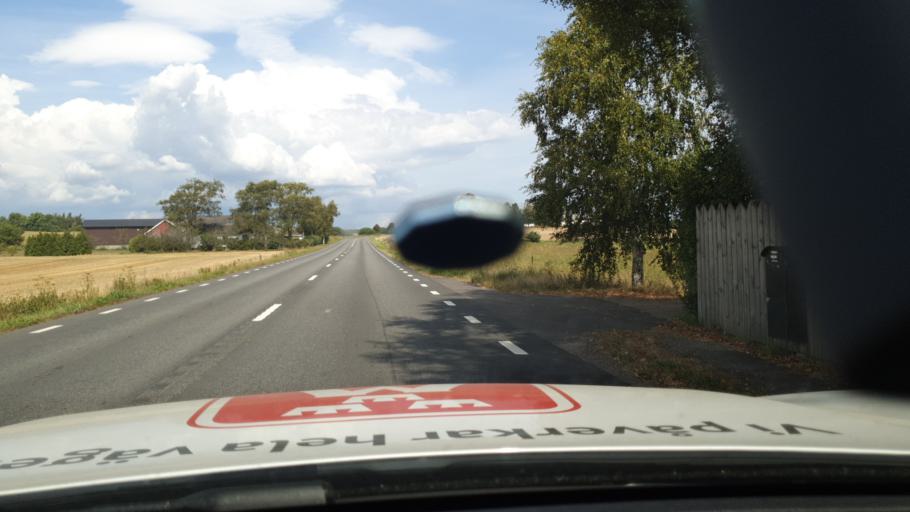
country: SE
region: Skane
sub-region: Simrishamns Kommun
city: Kivik
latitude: 55.5848
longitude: 14.1245
